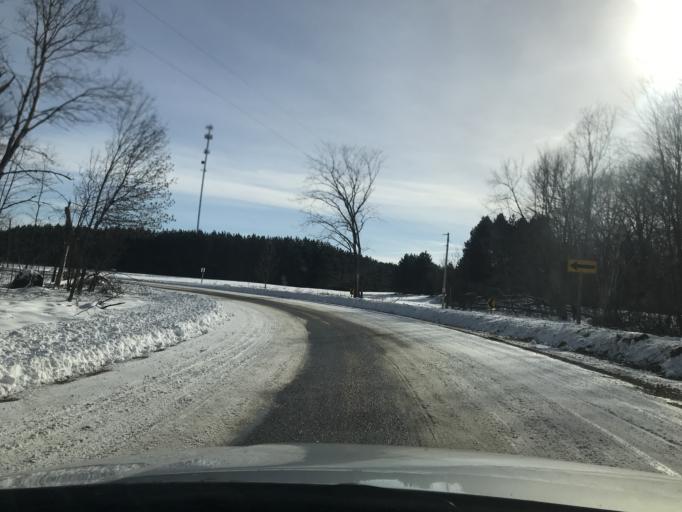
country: US
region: Wisconsin
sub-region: Oconto County
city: Gillett
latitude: 45.1207
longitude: -88.2499
